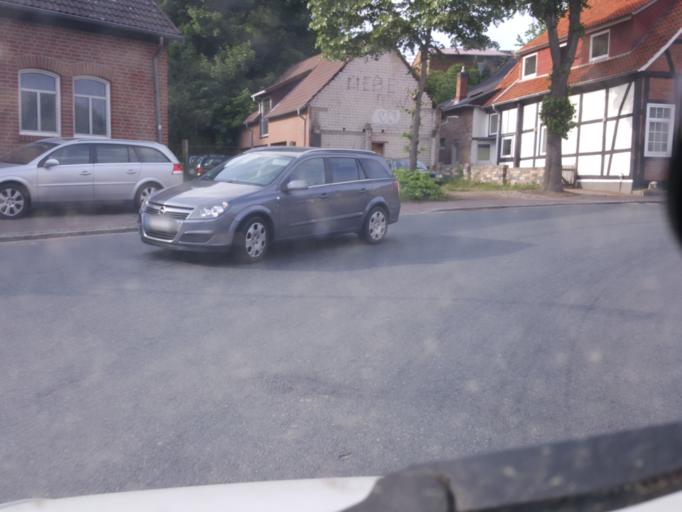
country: DE
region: Lower Saxony
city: Liebenau
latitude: 52.6060
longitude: 9.0915
